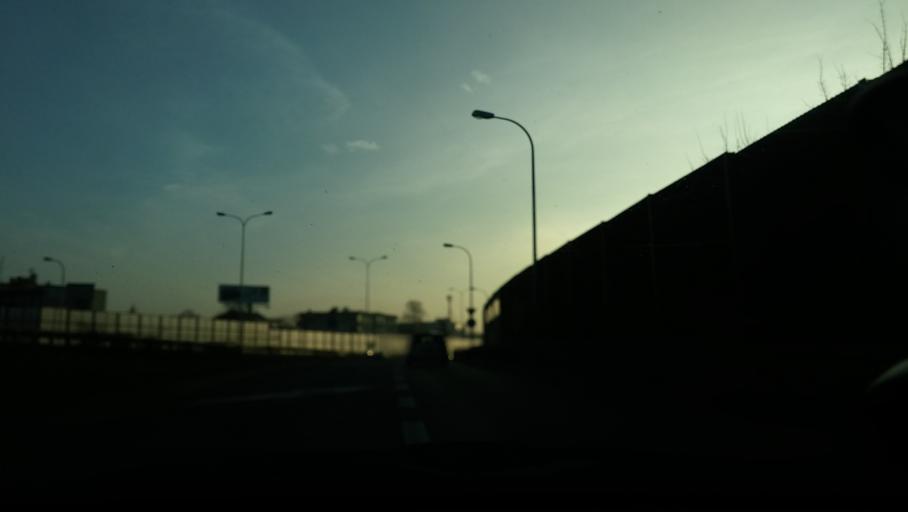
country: PL
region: Masovian Voivodeship
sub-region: Warszawa
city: Rembertow
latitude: 52.2322
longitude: 21.1304
